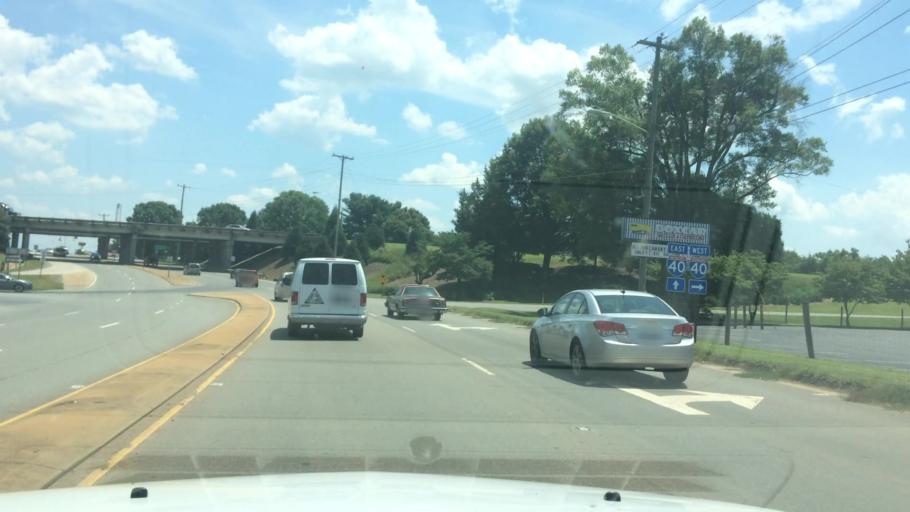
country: US
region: North Carolina
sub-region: Iredell County
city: Statesville
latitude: 35.7949
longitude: -80.9375
